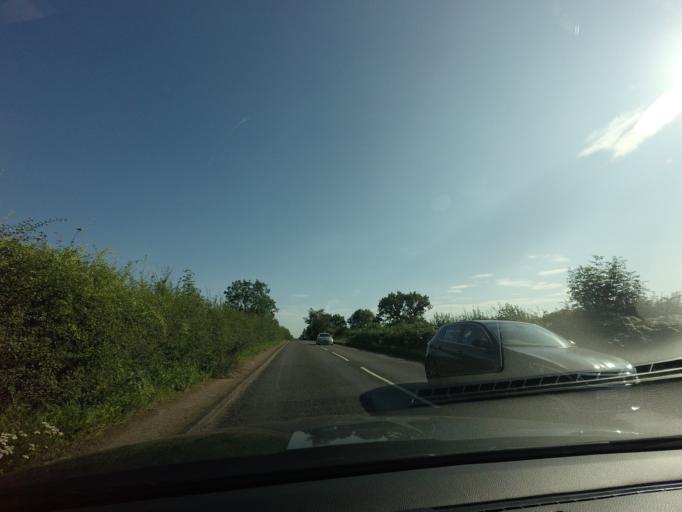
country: GB
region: England
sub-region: Nottinghamshire
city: Eastwood
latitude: 53.0440
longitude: -1.2977
